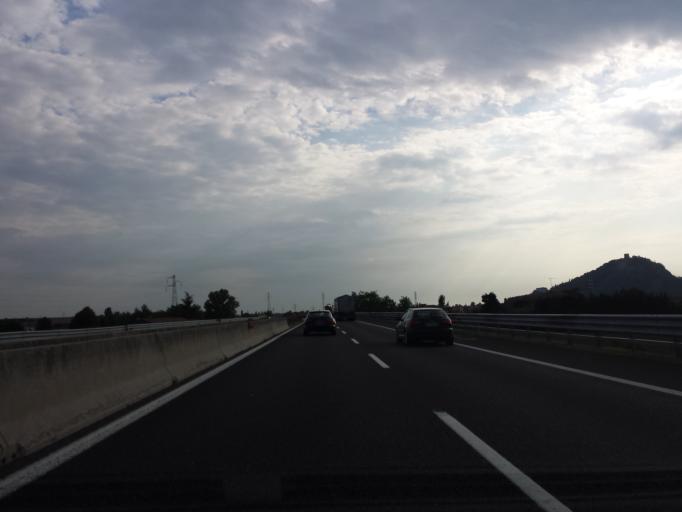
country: IT
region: Veneto
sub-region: Provincia di Padova
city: Pernumia
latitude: 45.2561
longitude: 11.7762
